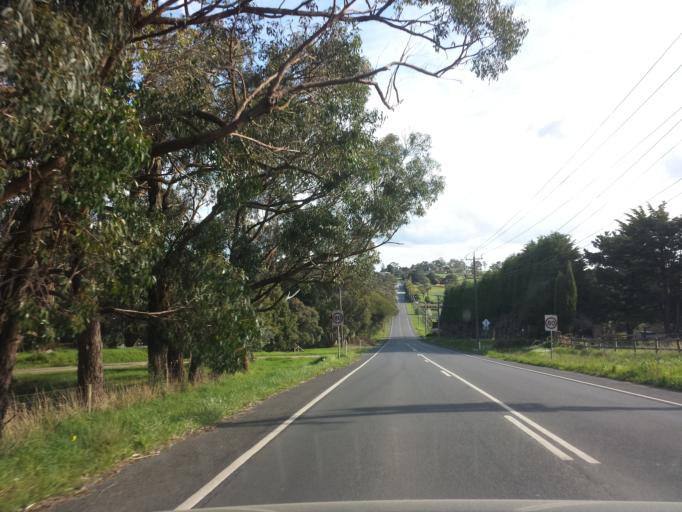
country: AU
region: Victoria
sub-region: Casey
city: Narre Warren North
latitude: -37.9760
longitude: 145.3596
